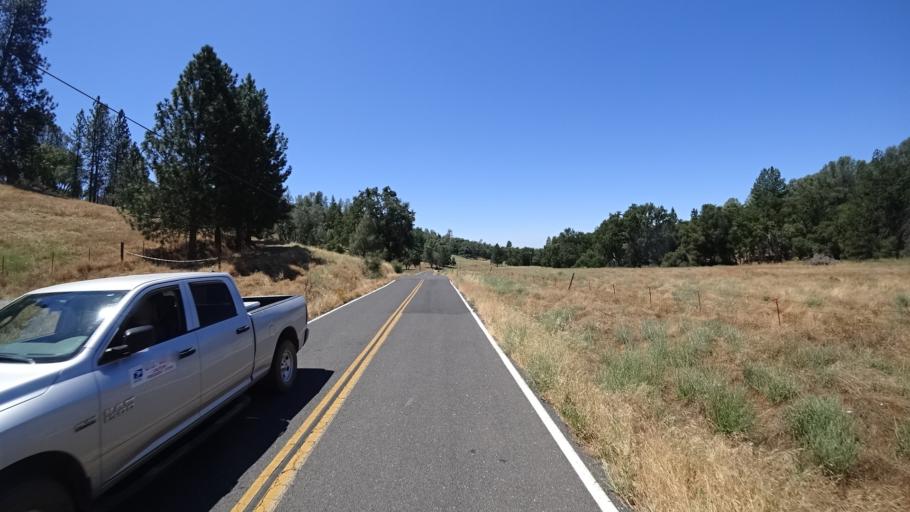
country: US
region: California
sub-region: Calaveras County
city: Mountain Ranch
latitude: 38.2076
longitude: -120.5519
